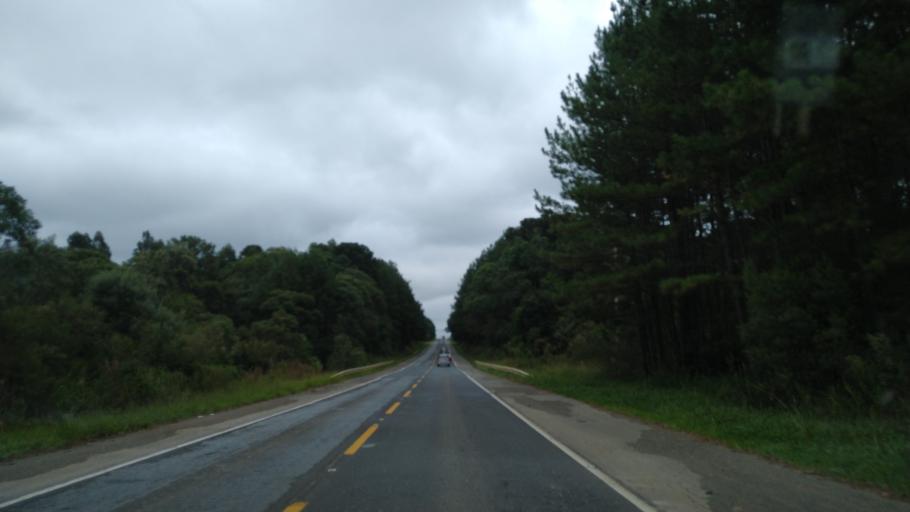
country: BR
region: Santa Catarina
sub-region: Tres Barras
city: Tres Barras
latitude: -26.1759
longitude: -50.1763
